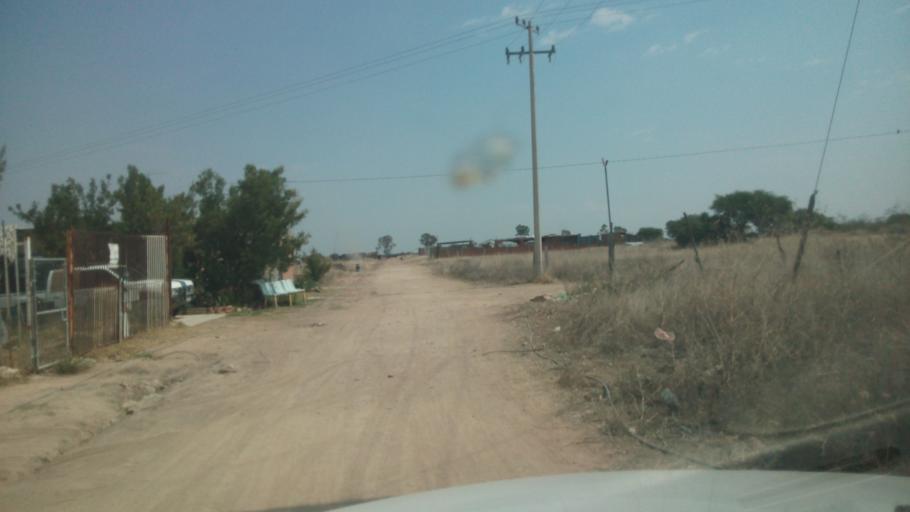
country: MX
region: Aguascalientes
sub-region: Aguascalientes
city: Villa Licenciado Jesus Teran (Calvillito)
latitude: 21.8437
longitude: -102.1651
